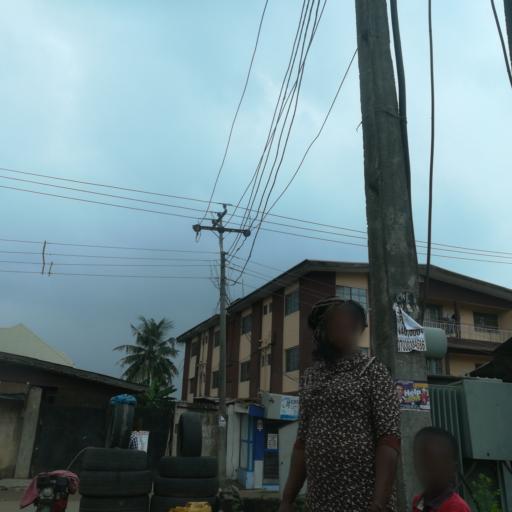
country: NG
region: Lagos
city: Agege
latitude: 6.5960
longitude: 3.2954
